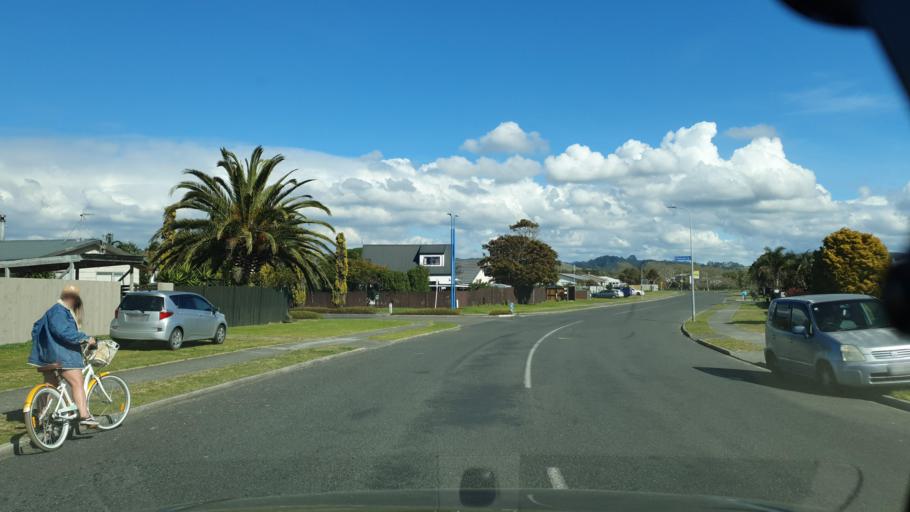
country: NZ
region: Bay of Plenty
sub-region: Tauranga City
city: Tauranga
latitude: -37.7029
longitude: 176.2936
